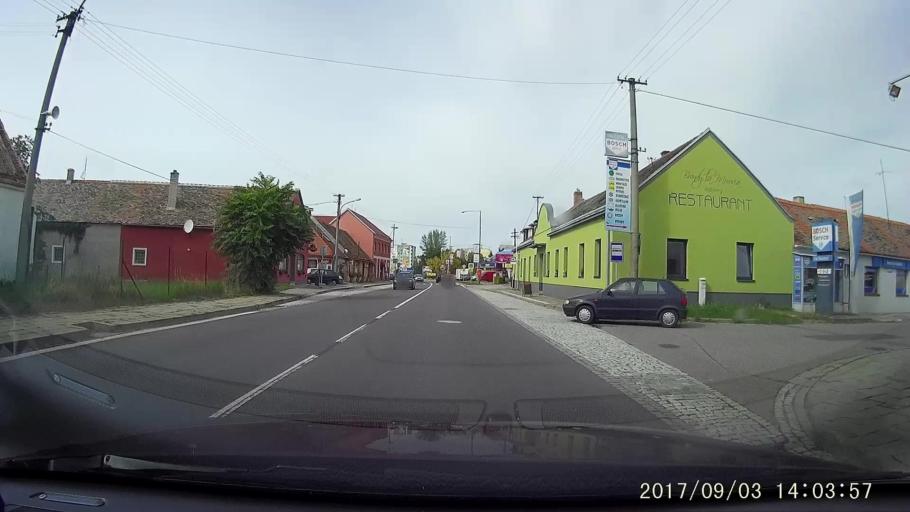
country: CZ
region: South Moravian
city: Dobsice
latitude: 48.8345
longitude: 16.0691
